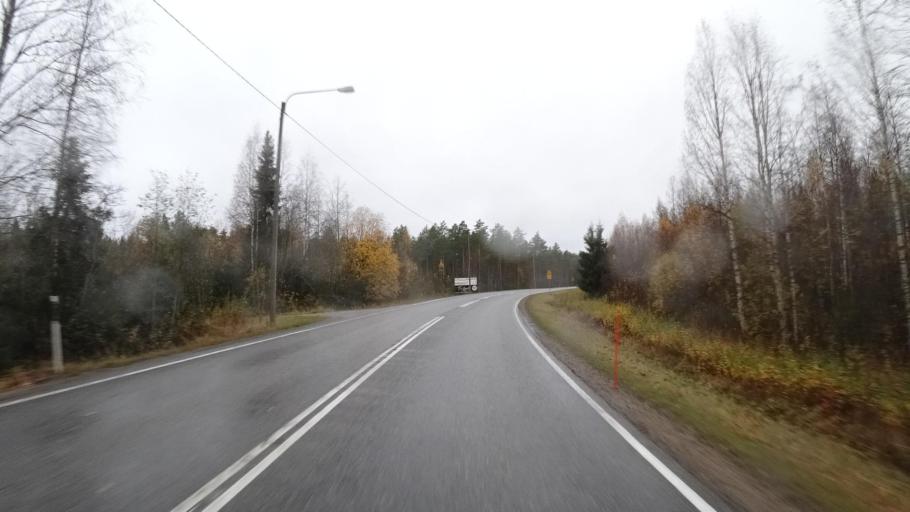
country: FI
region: Northern Savo
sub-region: Koillis-Savo
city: Tuusniemi
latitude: 62.7945
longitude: 28.5256
